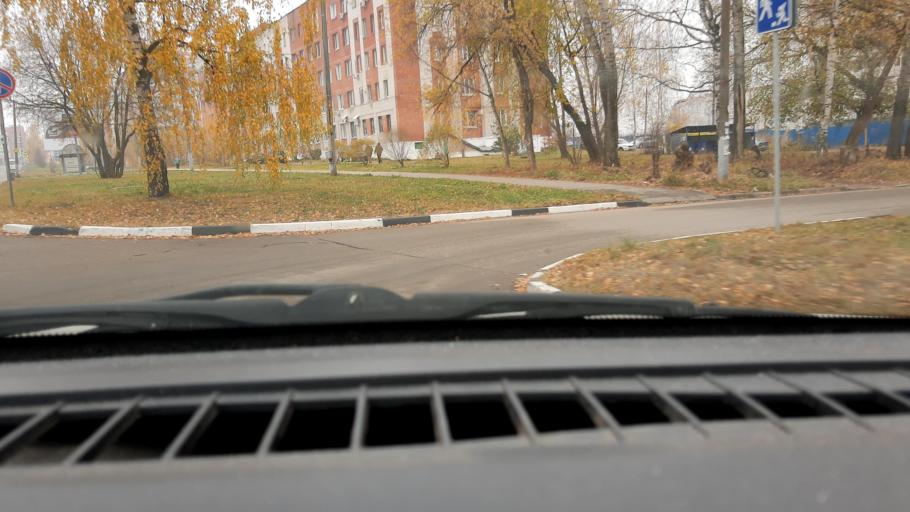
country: RU
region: Nizjnij Novgorod
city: Kstovo
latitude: 56.1497
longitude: 44.1845
